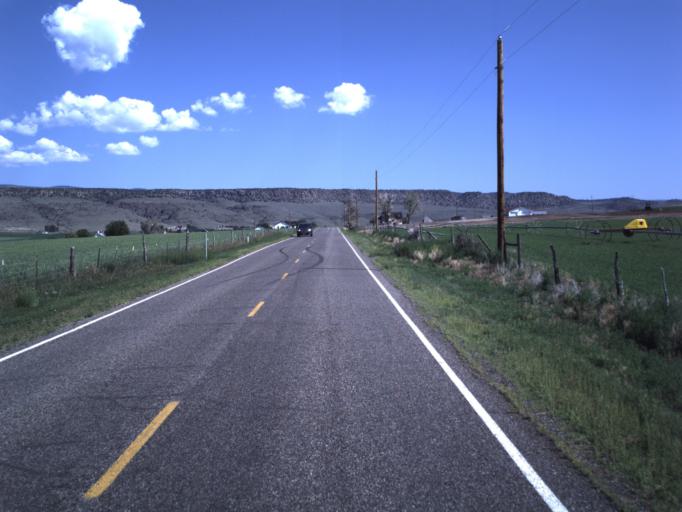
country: US
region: Utah
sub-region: Wayne County
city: Loa
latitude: 38.4292
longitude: -111.6202
